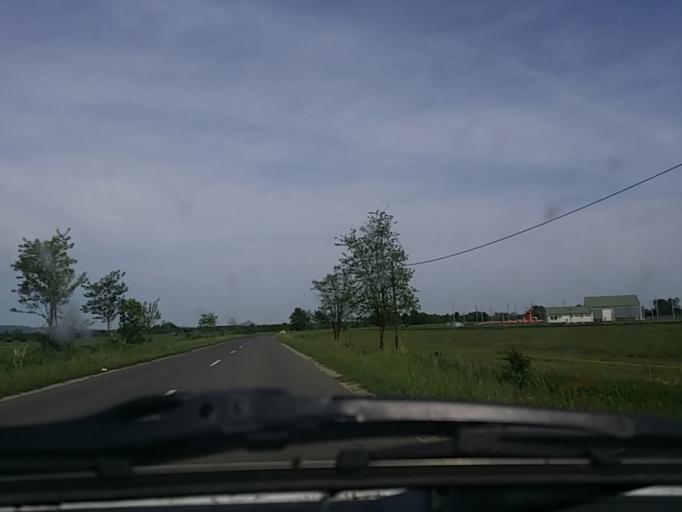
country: HU
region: Baranya
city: Harkany
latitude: 45.8415
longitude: 18.1479
